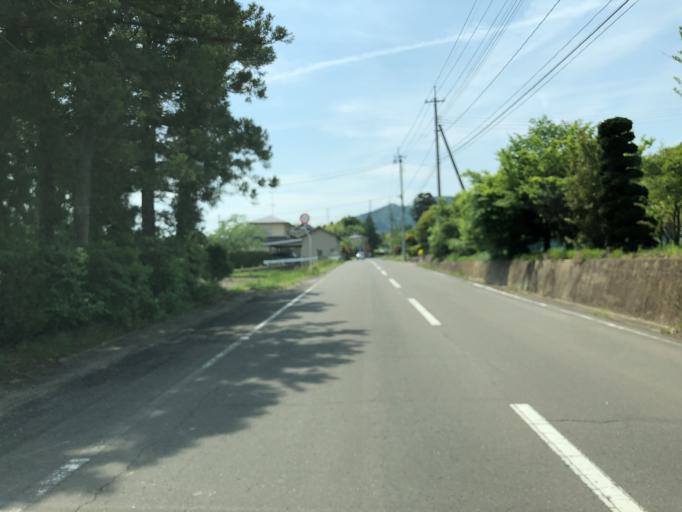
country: JP
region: Miyagi
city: Marumori
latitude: 37.8638
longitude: 140.8947
